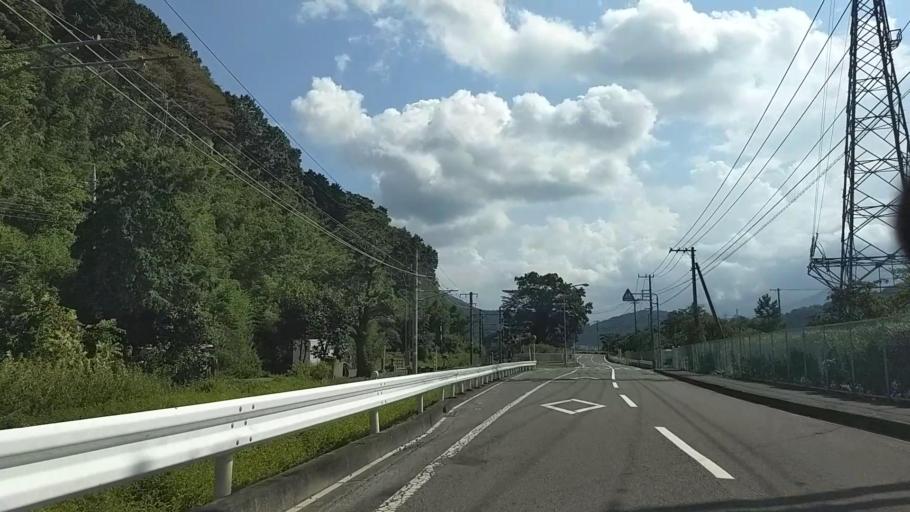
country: JP
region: Shizuoka
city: Fujinomiya
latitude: 35.3762
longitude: 138.4522
